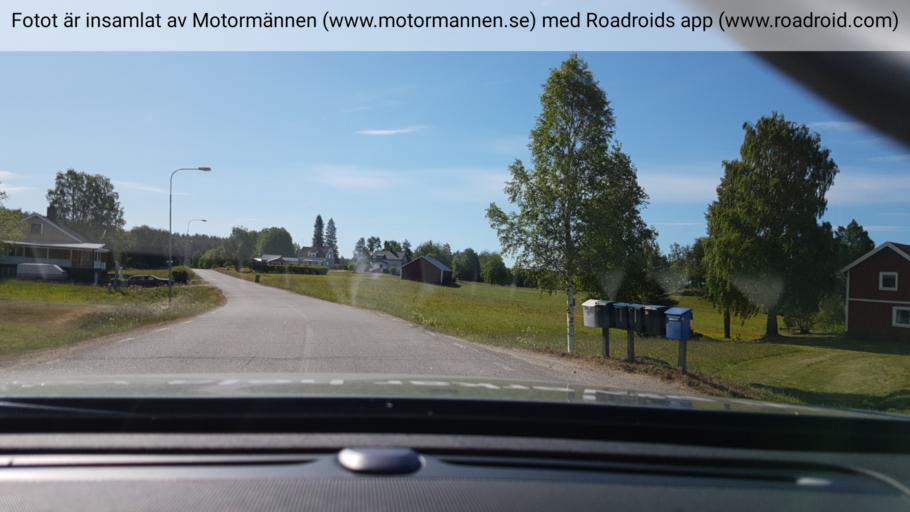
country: SE
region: Vaesterbotten
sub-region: Bjurholms Kommun
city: Bjurholm
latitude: 64.1182
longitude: 19.3131
